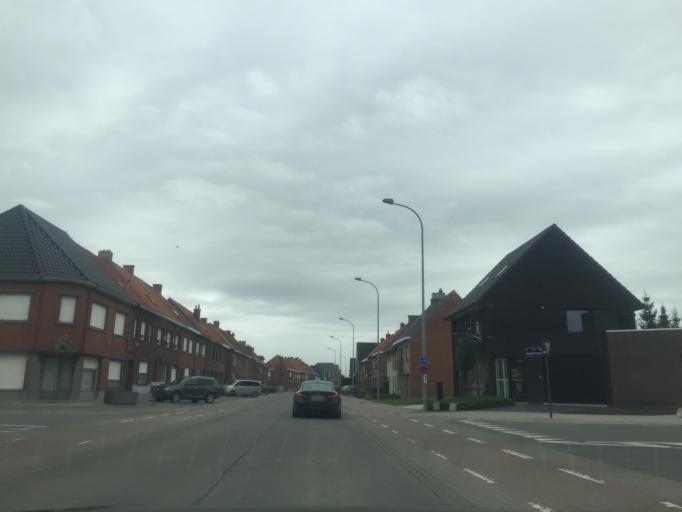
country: BE
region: Flanders
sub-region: Provincie West-Vlaanderen
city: Izegem
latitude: 50.9312
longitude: 3.2125
